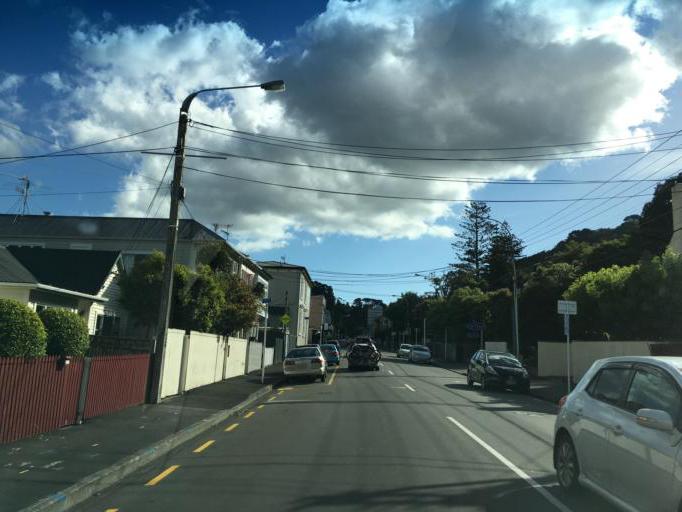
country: NZ
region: Wellington
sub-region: Wellington City
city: Kelburn
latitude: -41.2762
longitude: 174.7723
